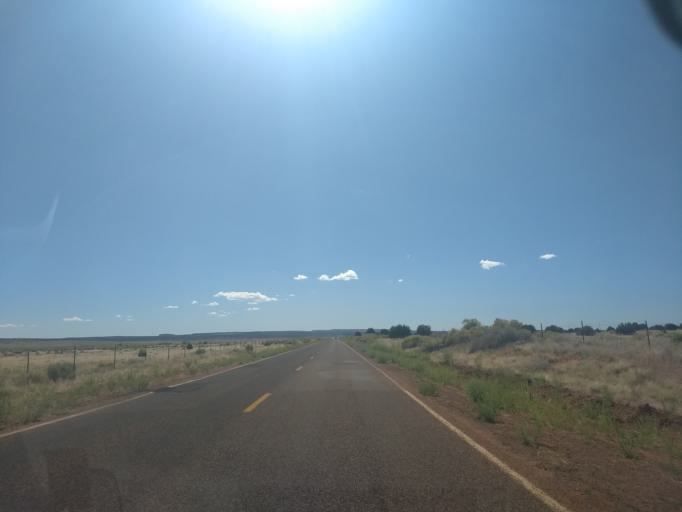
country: US
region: Arizona
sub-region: Mohave County
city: Colorado City
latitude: 36.9469
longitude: -112.9414
